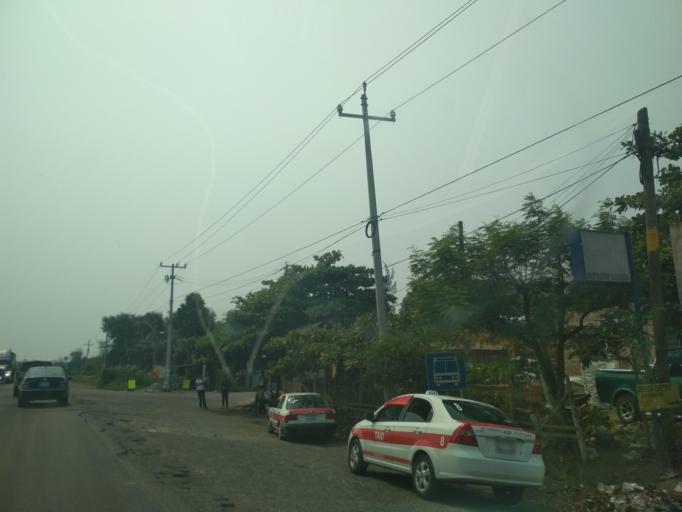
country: MX
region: Veracruz
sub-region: Veracruz
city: Delfino Victoria (Santa Fe)
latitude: 19.1944
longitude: -96.2893
